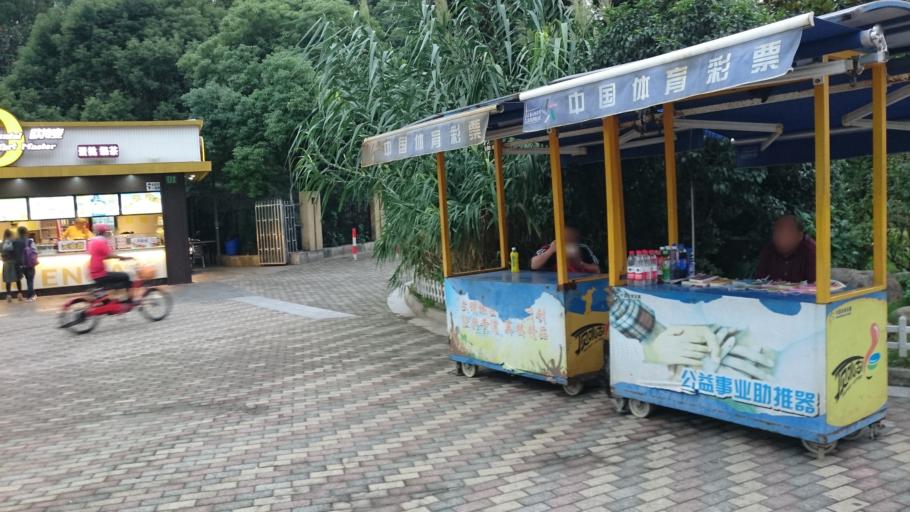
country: CN
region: Shanghai Shi
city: Shanghai
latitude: 31.2344
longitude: 121.4708
